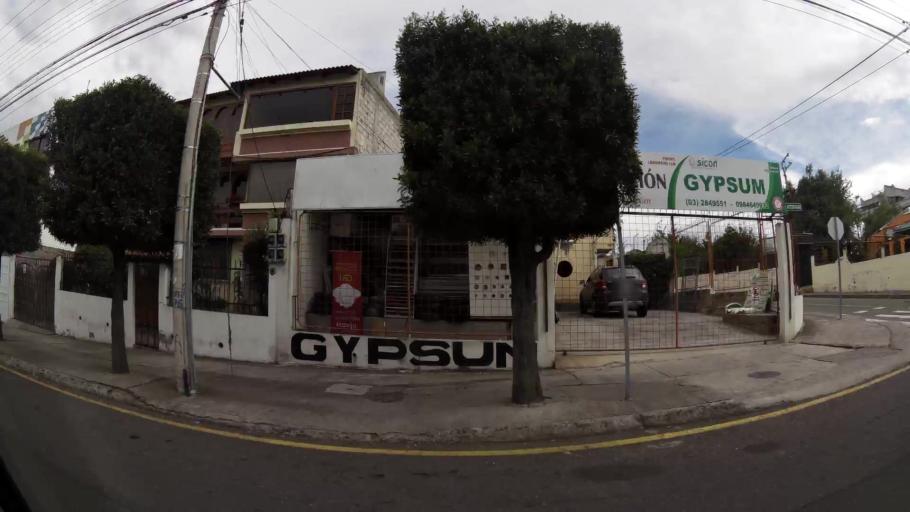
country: EC
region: Tungurahua
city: Ambato
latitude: -1.2671
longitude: -78.6321
